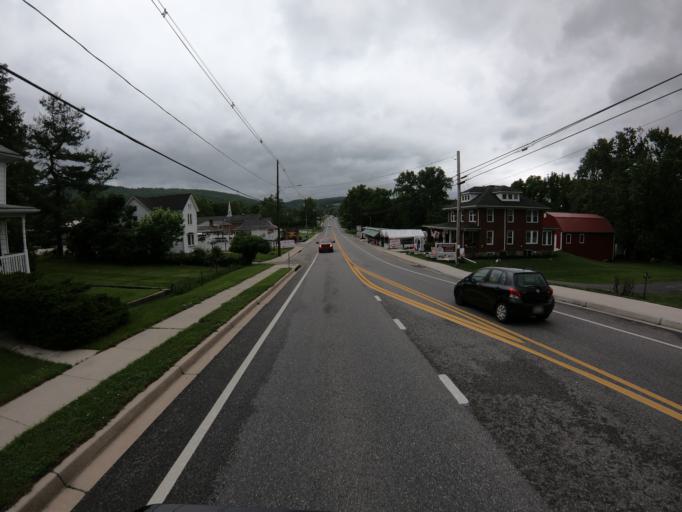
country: US
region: Maryland
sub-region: Washington County
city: Boonsboro
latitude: 39.5007
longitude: -77.6484
